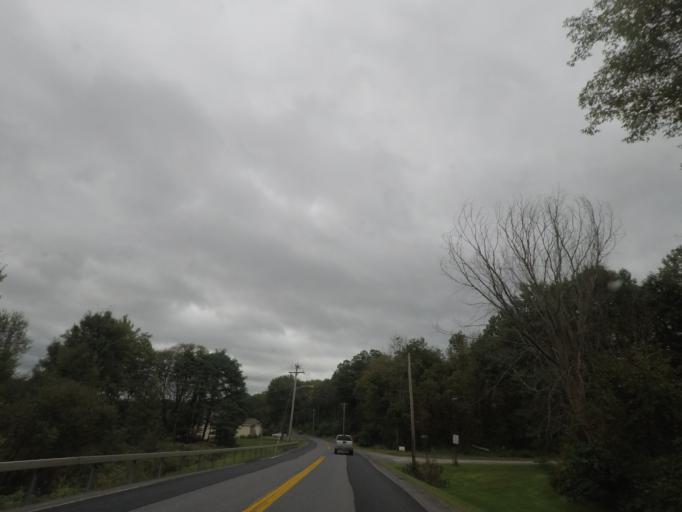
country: US
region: New York
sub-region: Rensselaer County
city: Hoosick Falls
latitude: 42.9505
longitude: -73.4057
